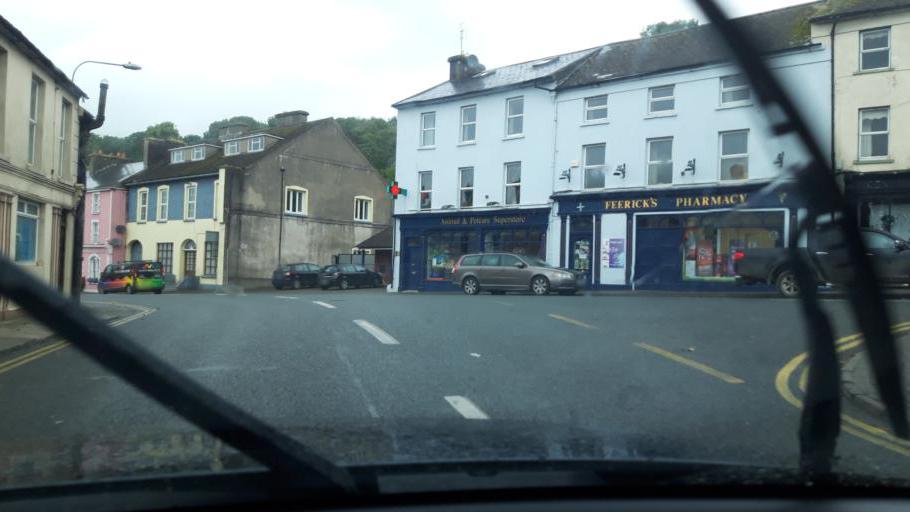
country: IE
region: Munster
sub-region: County Cork
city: Youghal
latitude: 52.1473
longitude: -7.8516
